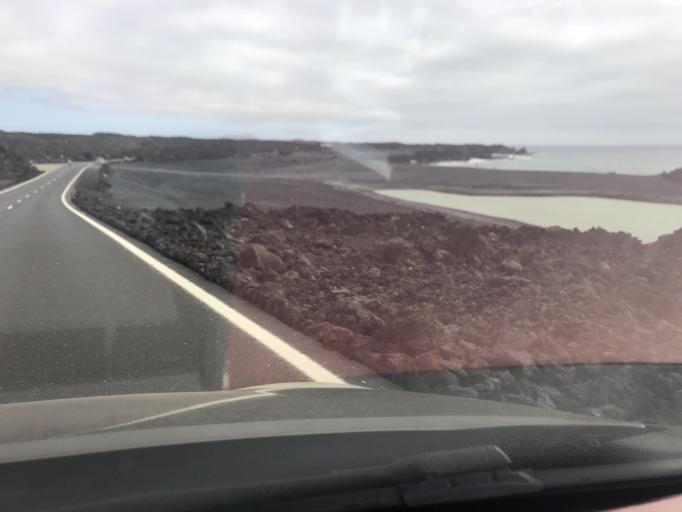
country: ES
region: Canary Islands
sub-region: Provincia de Las Palmas
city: Yaiza
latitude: 28.9621
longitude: -13.8289
